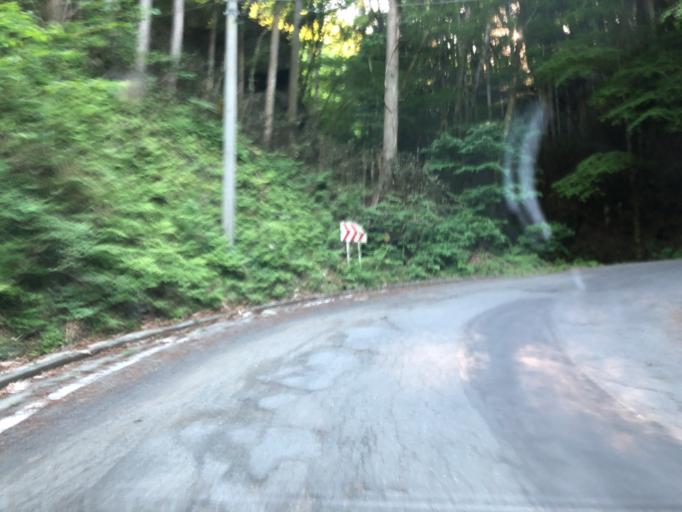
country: JP
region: Ibaraki
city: Kitaibaraki
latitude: 36.8894
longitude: 140.6228
